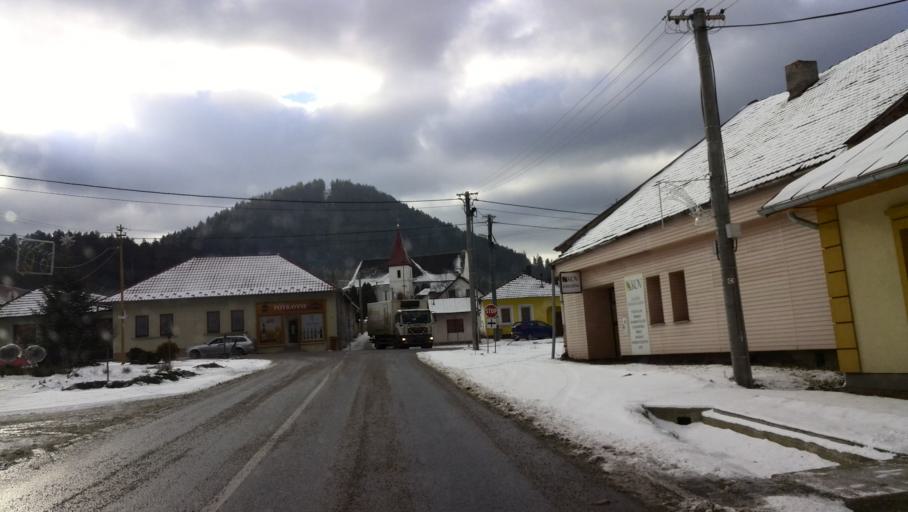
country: SK
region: Kosicky
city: Krompachy
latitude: 48.8047
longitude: 20.8052
